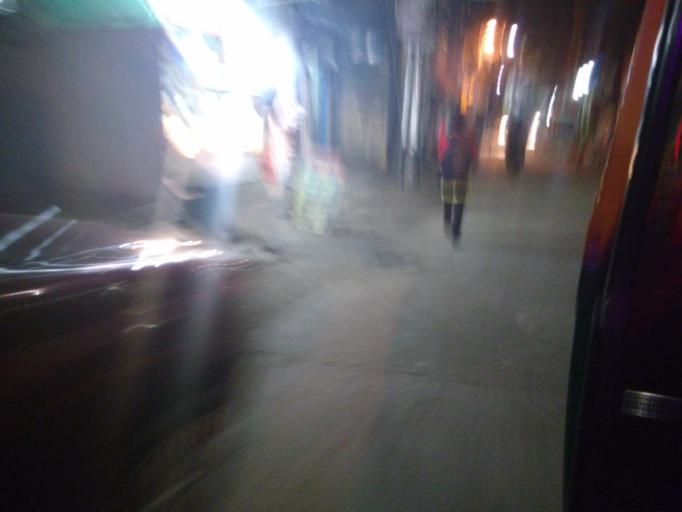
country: IN
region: West Bengal
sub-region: North 24 Parganas
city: Baranagar
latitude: 22.6346
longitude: 88.3659
